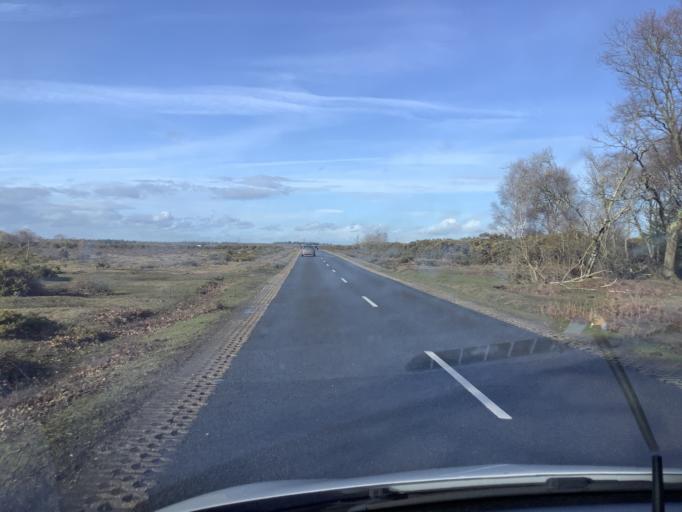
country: GB
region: England
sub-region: Hampshire
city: Hythe
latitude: 50.8292
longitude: -1.4311
